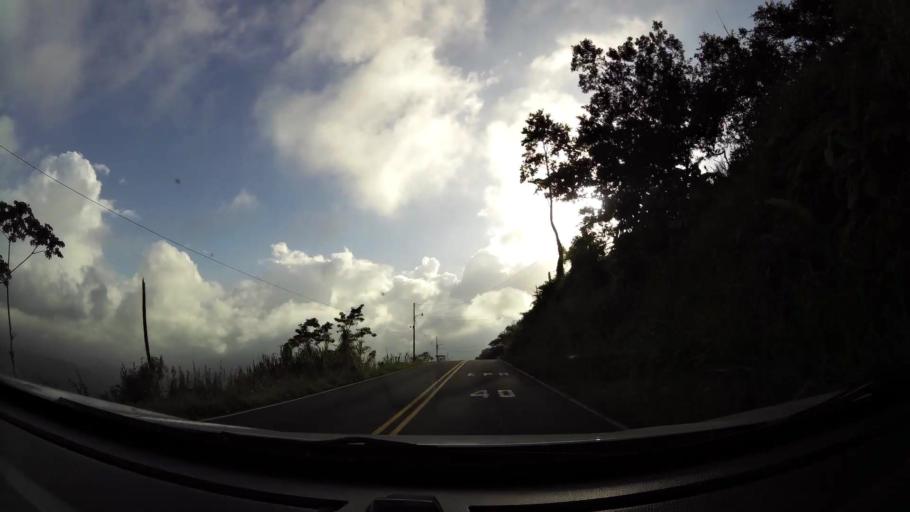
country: CR
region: Limon
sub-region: Canton de Siquirres
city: Siquirres
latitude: 10.0393
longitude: -83.5457
